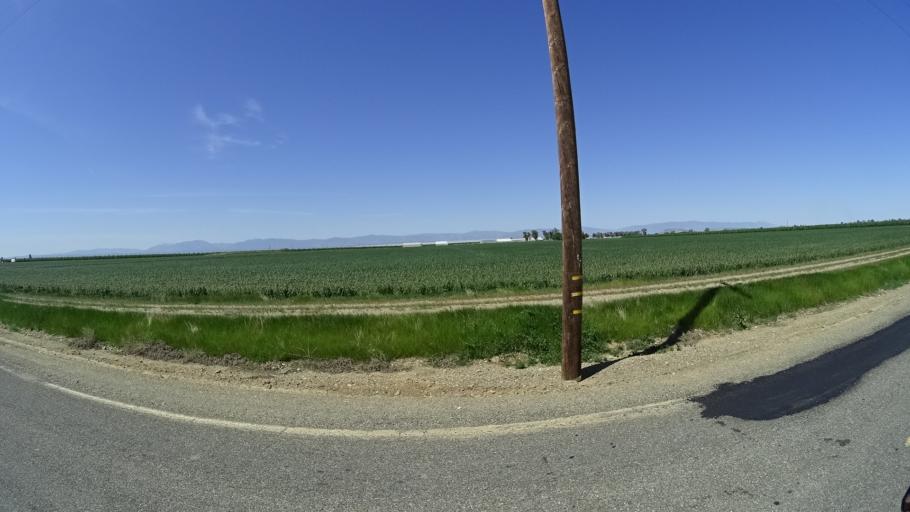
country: US
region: California
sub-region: Glenn County
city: Orland
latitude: 39.6791
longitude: -122.1781
